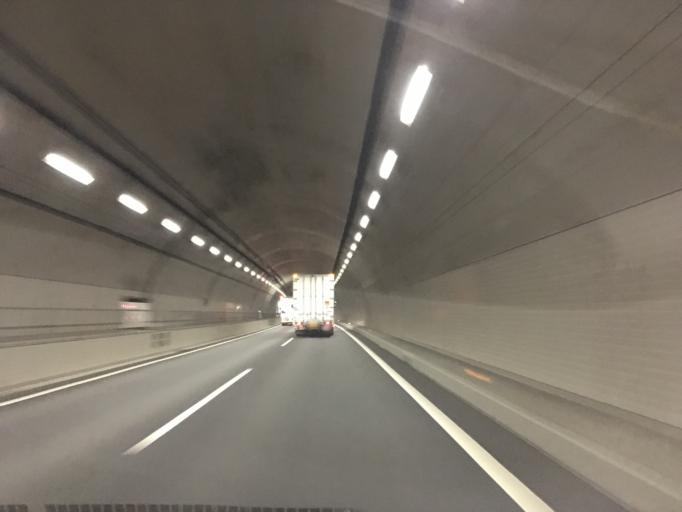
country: JP
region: Kanagawa
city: Zama
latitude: 35.5356
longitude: 139.3274
